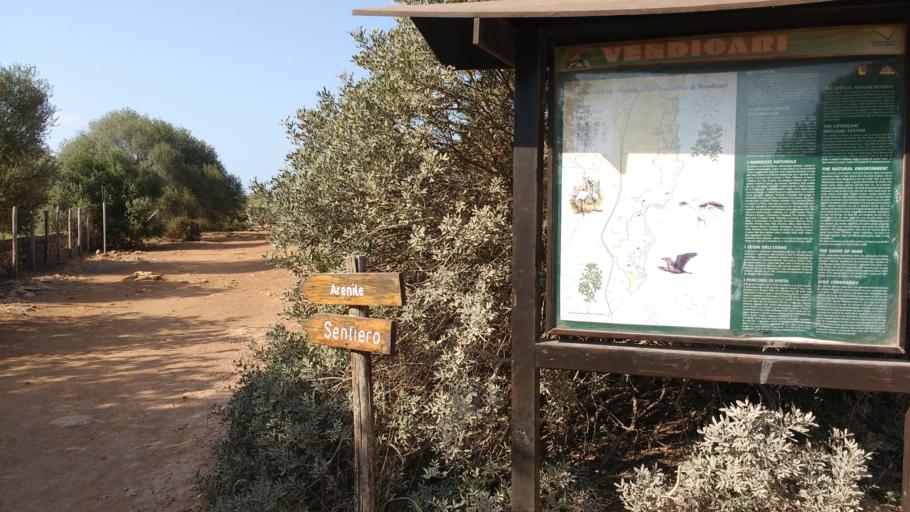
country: IT
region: Sicily
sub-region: Provincia di Siracusa
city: Noto
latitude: 36.8188
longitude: 15.0977
